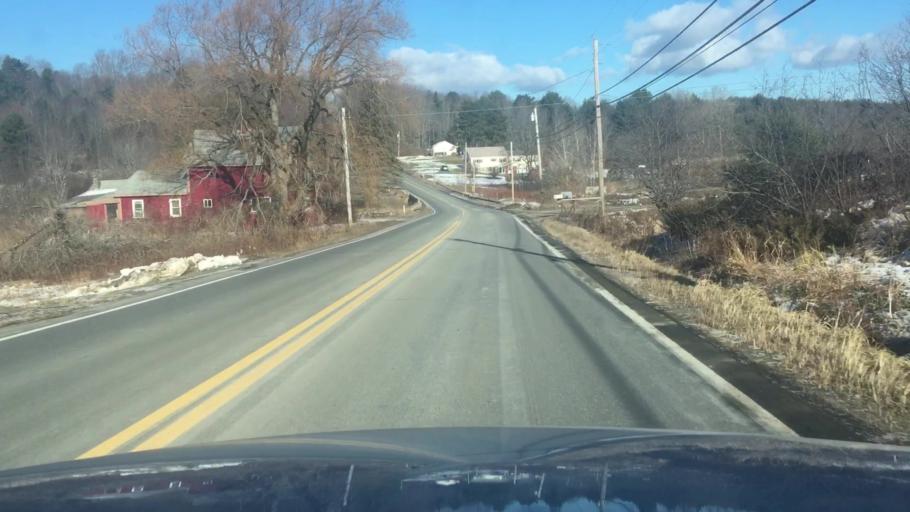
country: US
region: Maine
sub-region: Somerset County
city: Fairfield
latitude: 44.6491
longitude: -69.6760
